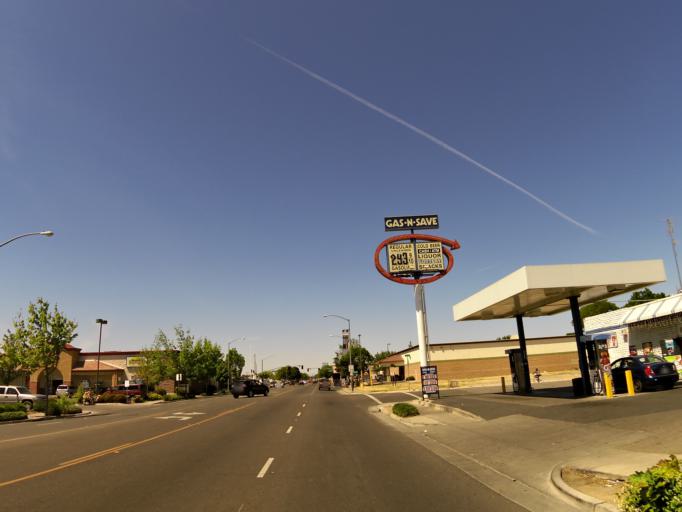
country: US
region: California
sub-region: Merced County
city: Merced
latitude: 37.3031
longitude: -120.4910
